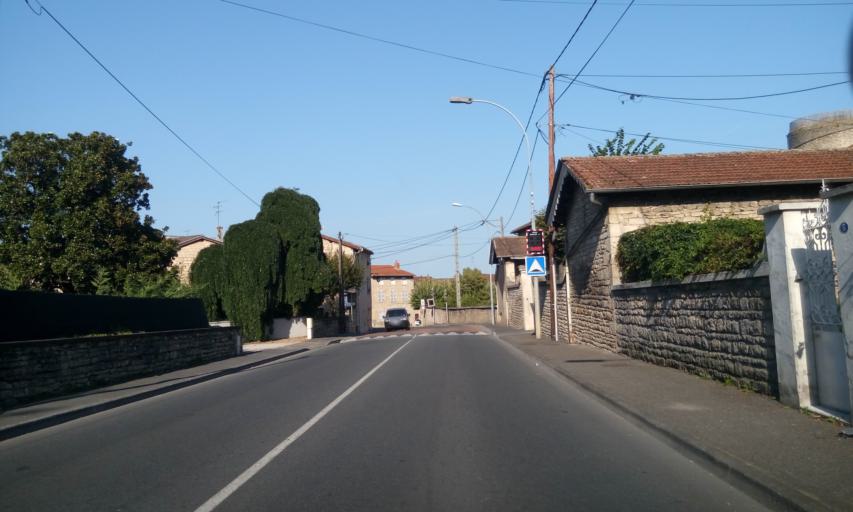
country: FR
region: Rhone-Alpes
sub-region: Departement du Rhone
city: Anse
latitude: 45.9341
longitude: 4.7174
